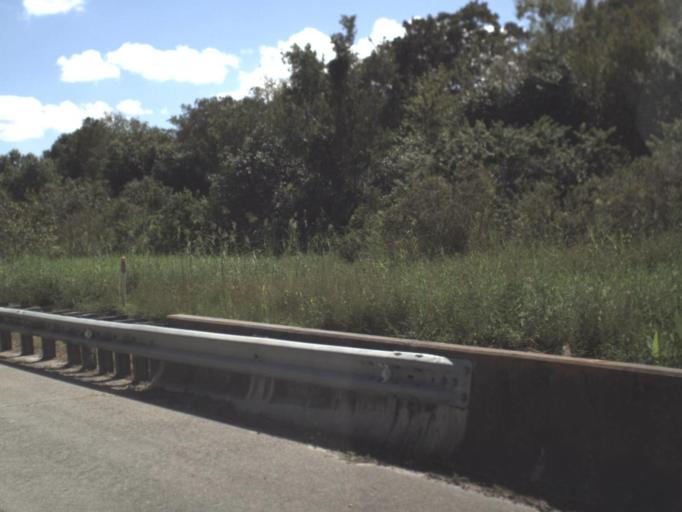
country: US
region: Florida
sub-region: Collier County
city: Lely Resort
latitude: 26.0208
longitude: -81.6327
